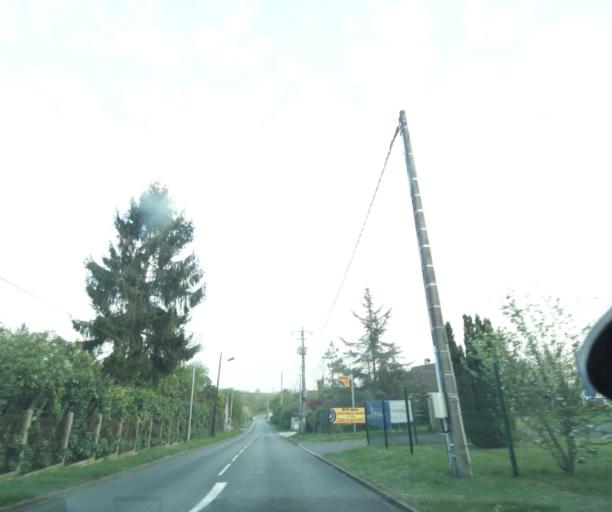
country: FR
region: Ile-de-France
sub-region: Departement de Seine-et-Marne
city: Montigny-sur-Loing
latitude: 48.3453
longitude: 2.7714
